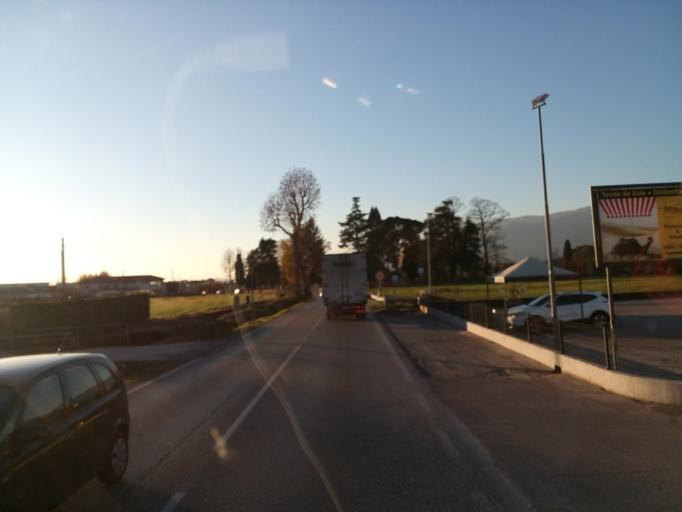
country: IT
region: Veneto
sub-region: Provincia di Vicenza
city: Romano d'Ezzelino
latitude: 45.7794
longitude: 11.7850
